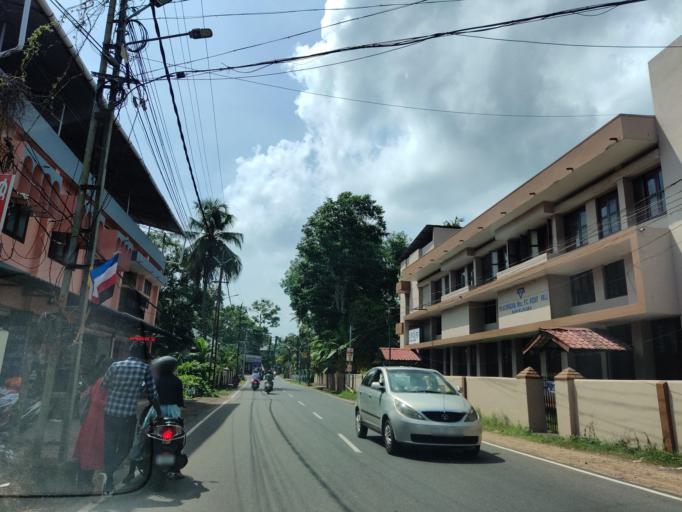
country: IN
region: Kerala
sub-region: Alappuzha
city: Mavelikara
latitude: 9.2546
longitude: 76.5453
